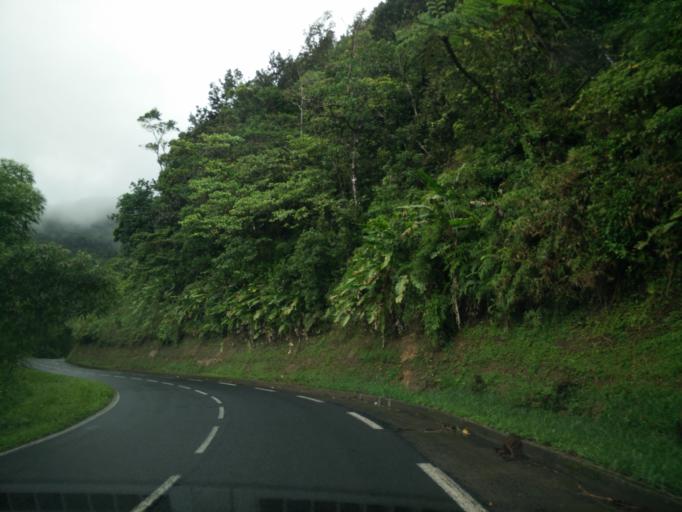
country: MQ
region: Martinique
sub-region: Martinique
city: Le Morne-Rouge
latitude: 14.7387
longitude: -61.1013
